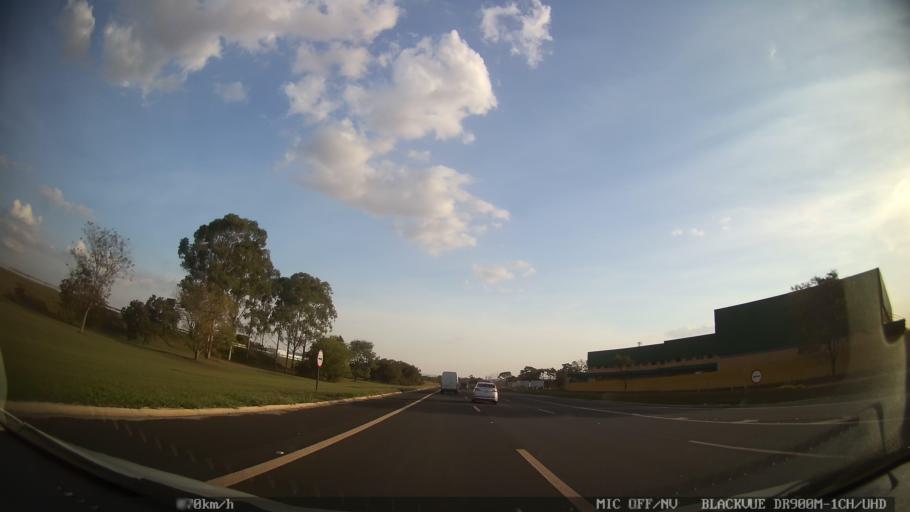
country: BR
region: Sao Paulo
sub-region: Ribeirao Preto
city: Ribeirao Preto
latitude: -21.1137
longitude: -47.7815
